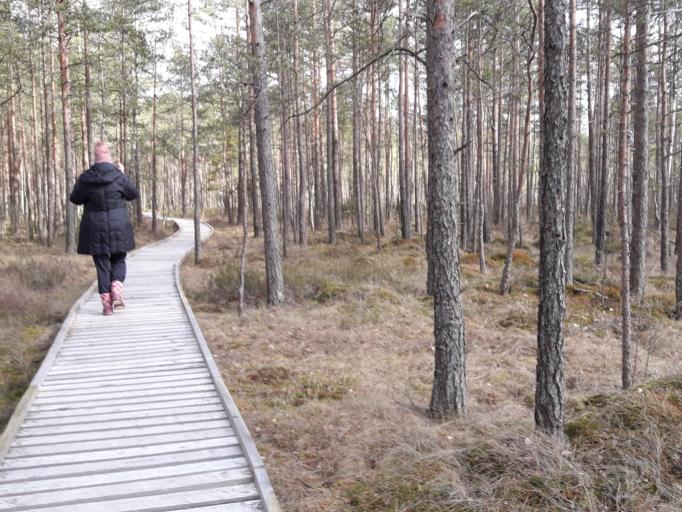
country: LV
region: Talsu Rajons
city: Sabile
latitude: 56.9070
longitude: 22.3931
